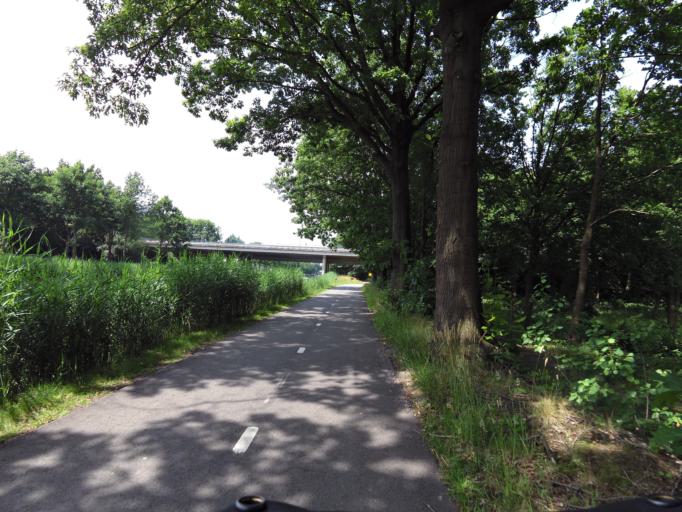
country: NL
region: Gelderland
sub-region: Gemeente Apeldoorn
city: Loenen
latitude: 52.1571
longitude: 6.0187
